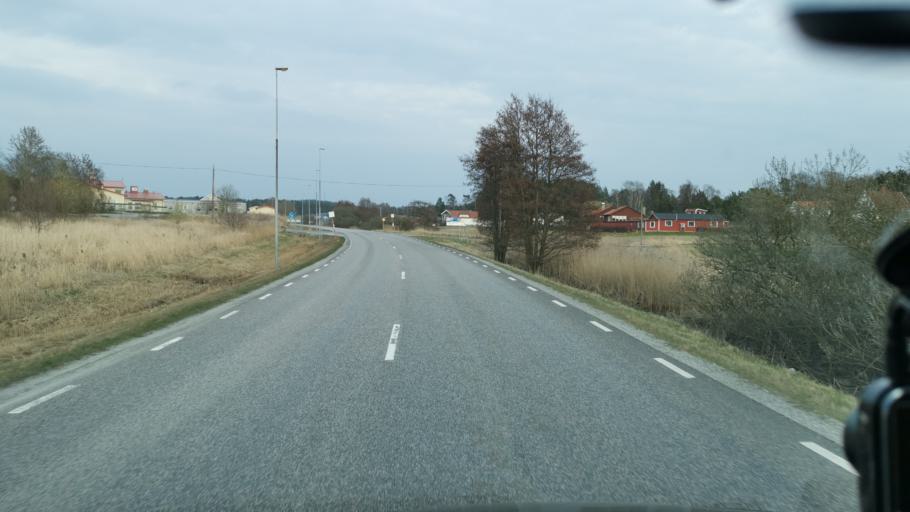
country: SE
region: Vaestra Goetaland
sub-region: Kungalvs Kommun
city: Kode
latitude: 57.9380
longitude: 11.8418
